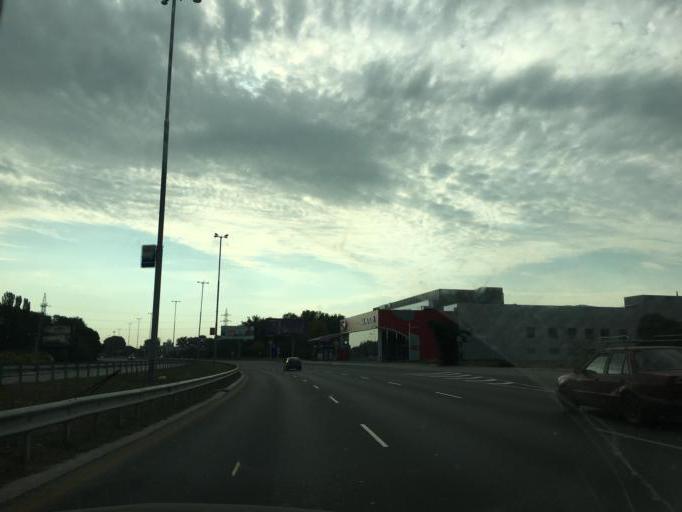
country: BG
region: Sofia-Capital
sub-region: Stolichna Obshtina
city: Sofia
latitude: 42.6377
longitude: 23.4140
